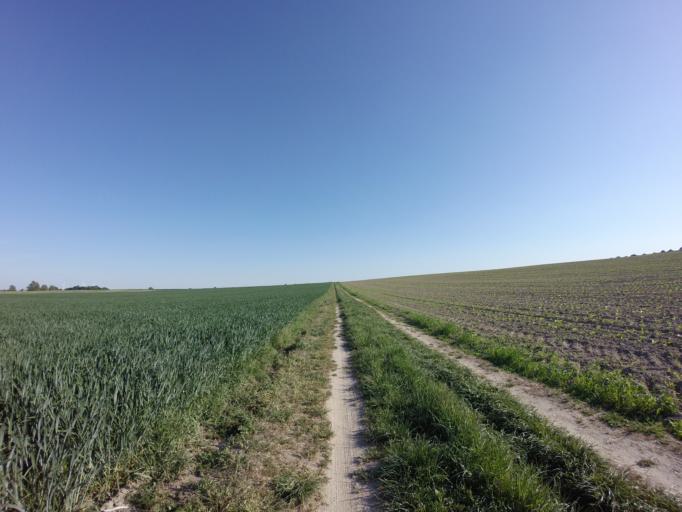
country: PL
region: West Pomeranian Voivodeship
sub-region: Powiat choszczenski
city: Choszczno
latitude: 53.1449
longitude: 15.3861
